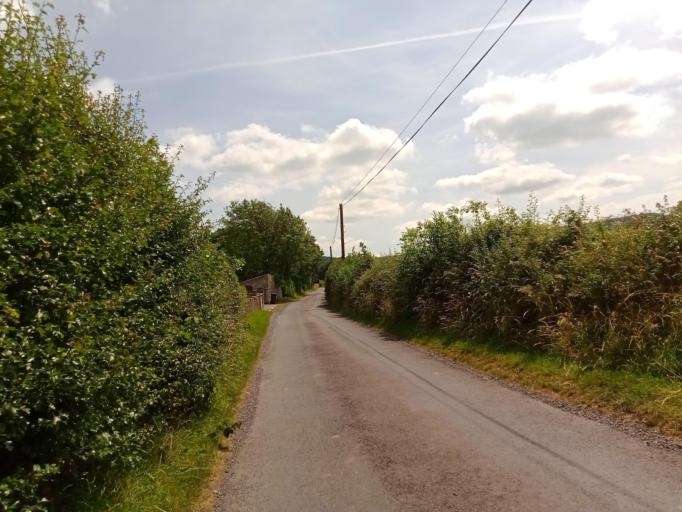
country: IE
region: Leinster
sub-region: Laois
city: Rathdowney
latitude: 52.8140
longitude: -7.4711
